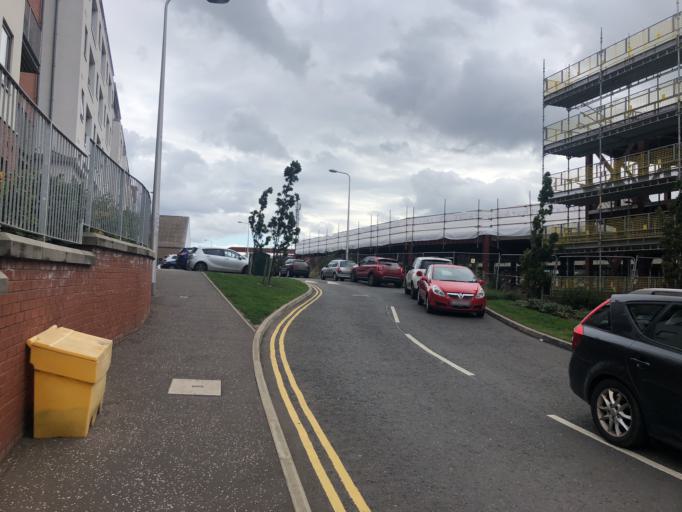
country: GB
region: Scotland
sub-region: West Lothian
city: Seafield
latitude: 55.9738
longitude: -3.1614
